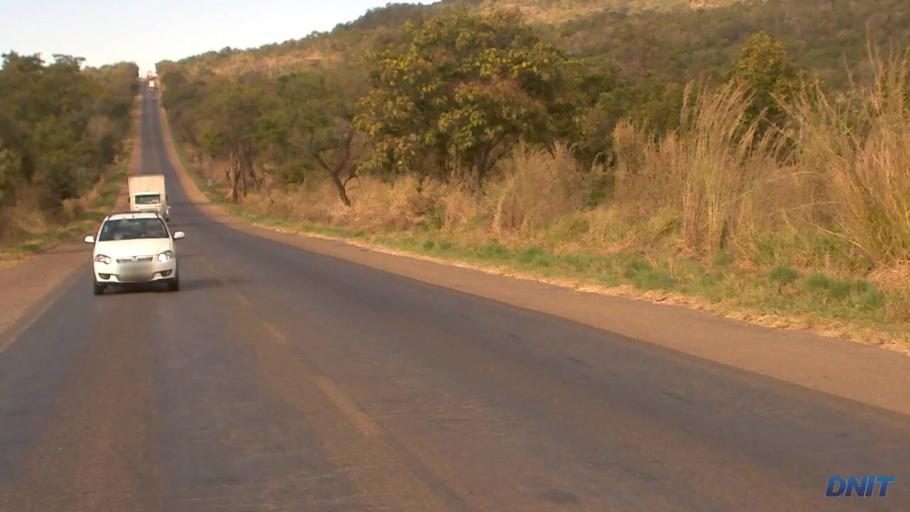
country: BR
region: Goias
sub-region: Uruacu
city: Uruacu
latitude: -14.5485
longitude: -49.1602
